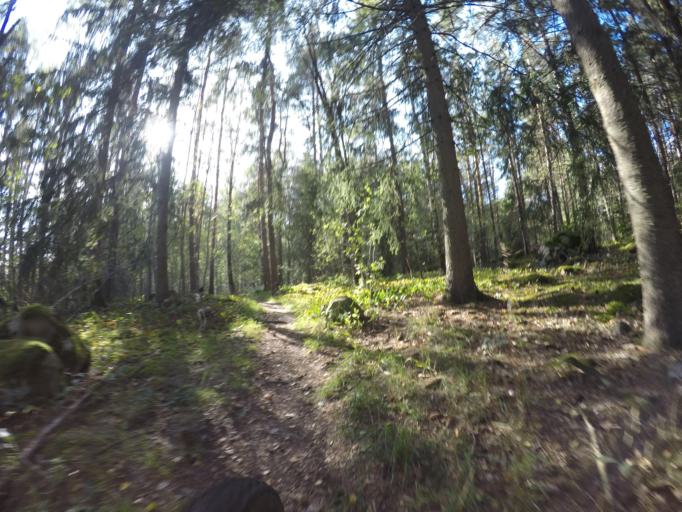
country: SE
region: Vaestmanland
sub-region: Kopings Kommun
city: Koping
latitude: 59.5071
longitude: 16.0280
